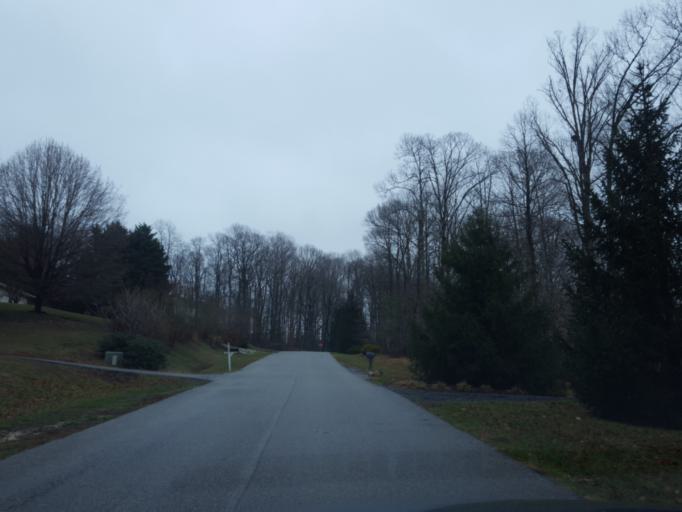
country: US
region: Maryland
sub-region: Calvert County
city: Huntingtown
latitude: 38.6072
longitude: -76.5402
